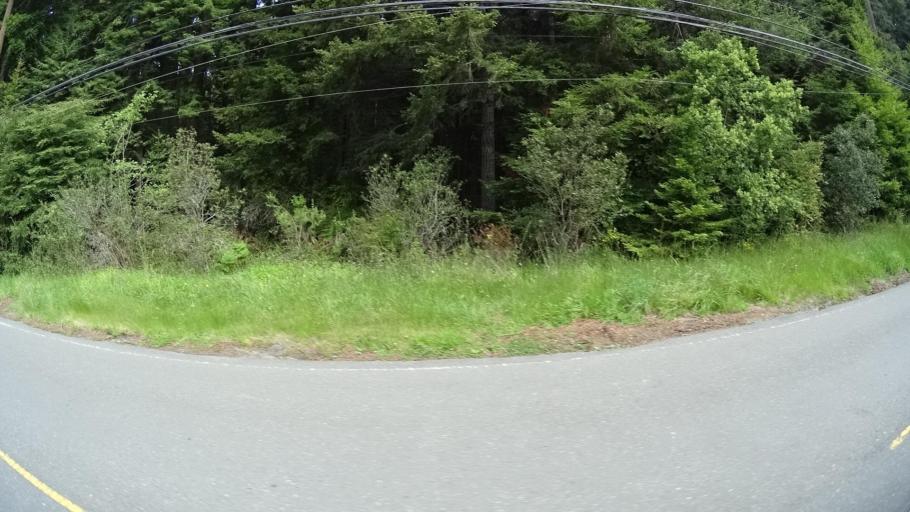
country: US
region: California
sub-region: Humboldt County
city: Arcata
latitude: 40.8687
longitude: -124.0682
